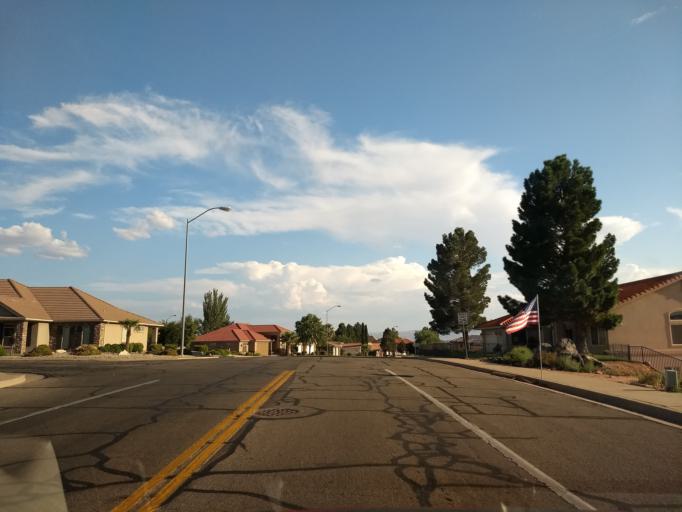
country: US
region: Utah
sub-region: Washington County
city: Saint George
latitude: 37.1110
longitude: -113.5515
